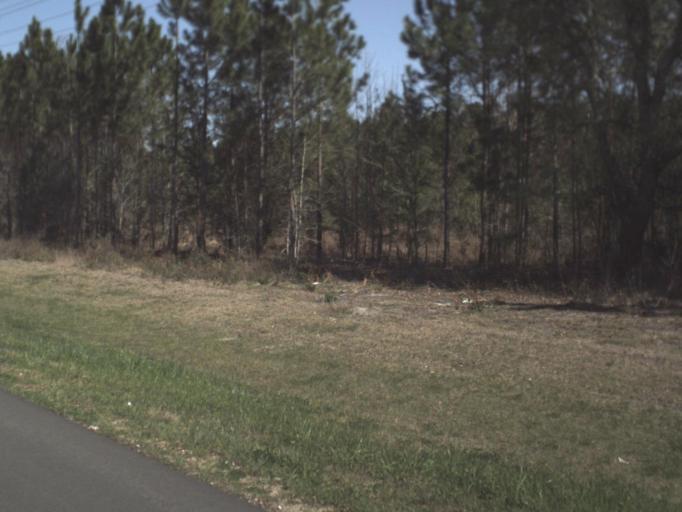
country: US
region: Florida
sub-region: Jackson County
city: Sneads
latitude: 30.7310
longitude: -85.0200
